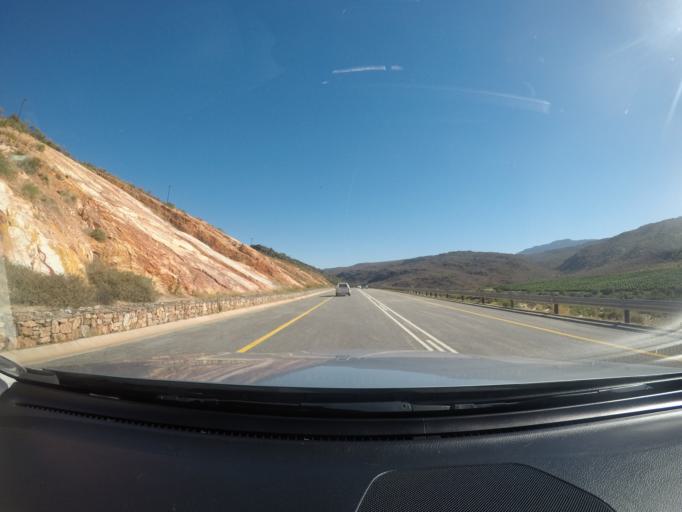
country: ZA
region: Western Cape
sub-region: West Coast District Municipality
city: Clanwilliam
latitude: -32.4190
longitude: 18.9565
